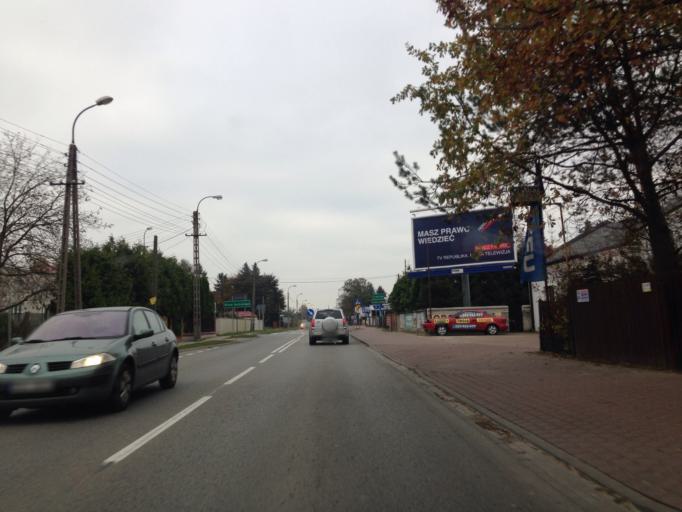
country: PL
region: Masovian Voivodeship
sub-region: Powiat warszawski zachodni
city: Babice
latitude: 52.2441
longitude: 20.8626
